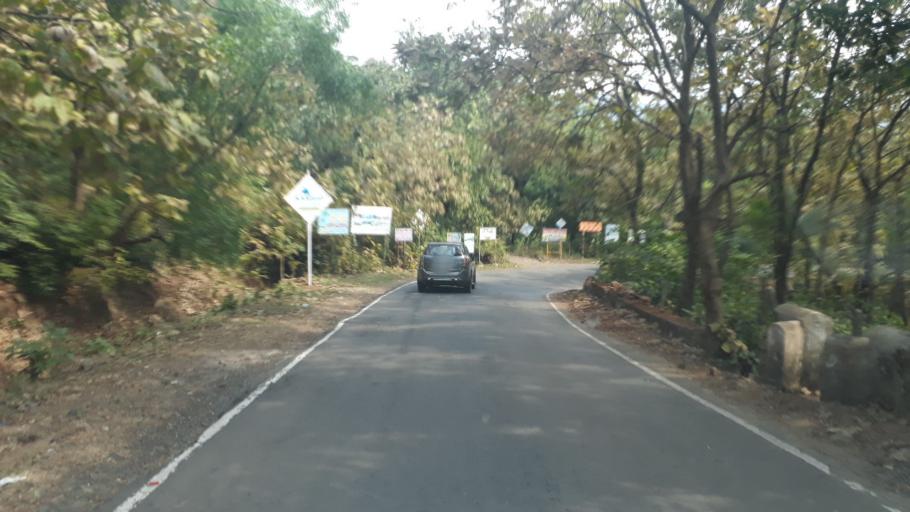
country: IN
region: Maharashtra
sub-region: Raigarh
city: Revadanda
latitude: 18.4596
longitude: 72.8965
